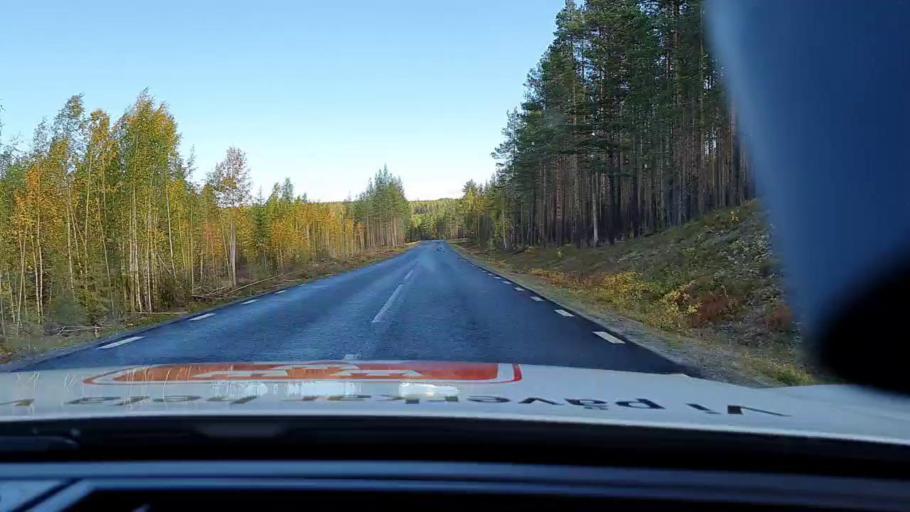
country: SE
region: Vaesterbotten
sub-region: Skelleftea Kommun
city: Langsele
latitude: 64.9504
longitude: 20.0249
